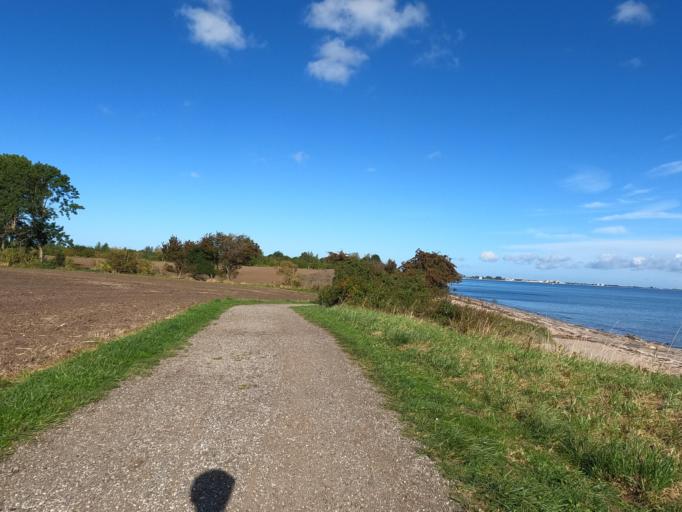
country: DE
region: Schleswig-Holstein
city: Neukirchen
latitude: 54.3175
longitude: 11.0737
